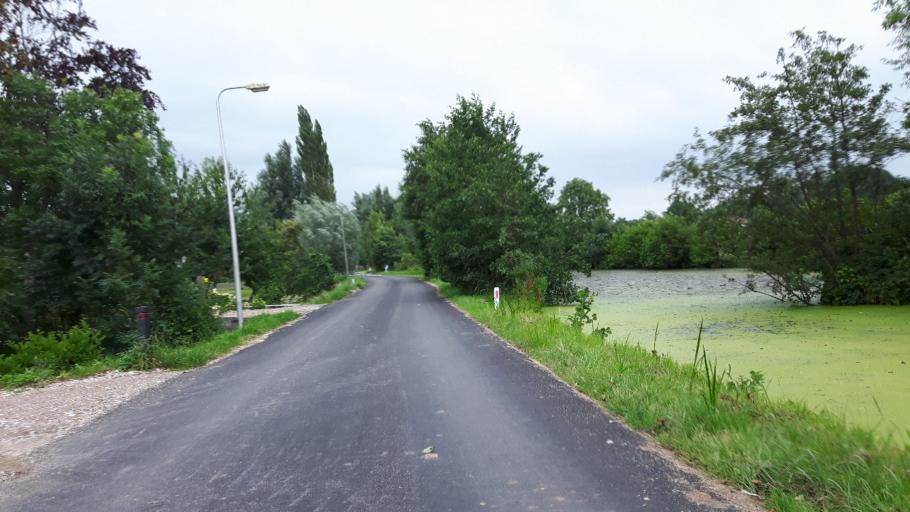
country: NL
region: South Holland
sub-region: Bodegraven-Reeuwijk
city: Bodegraven
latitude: 52.1111
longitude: 4.7142
